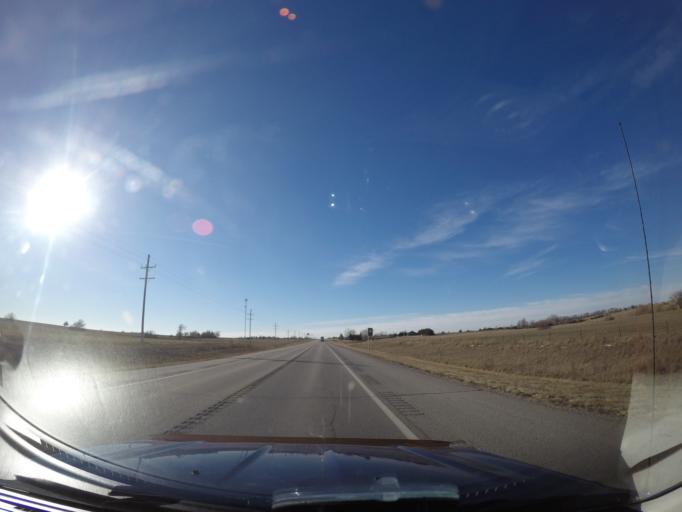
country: US
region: Kansas
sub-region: Marion County
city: Hillsboro
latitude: 38.3627
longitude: -97.2322
